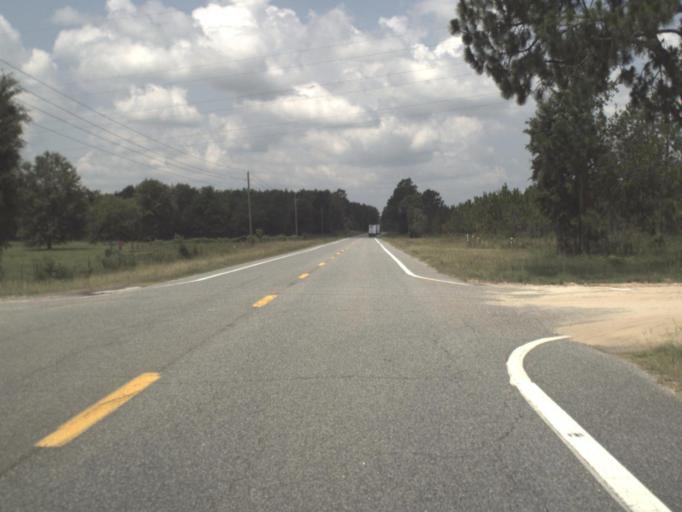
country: US
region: Florida
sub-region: Hamilton County
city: Jasper
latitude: 30.4874
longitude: -83.1781
